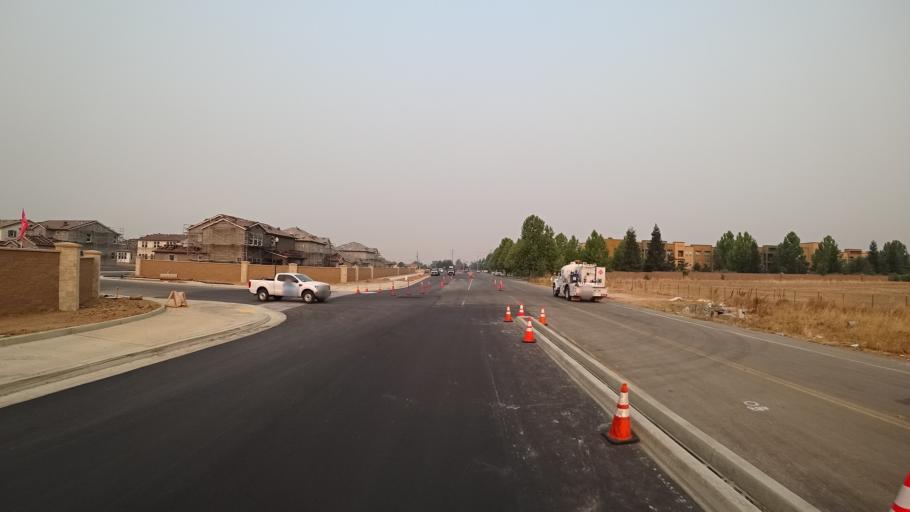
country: US
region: California
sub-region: Sacramento County
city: Laguna
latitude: 38.3795
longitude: -121.4143
